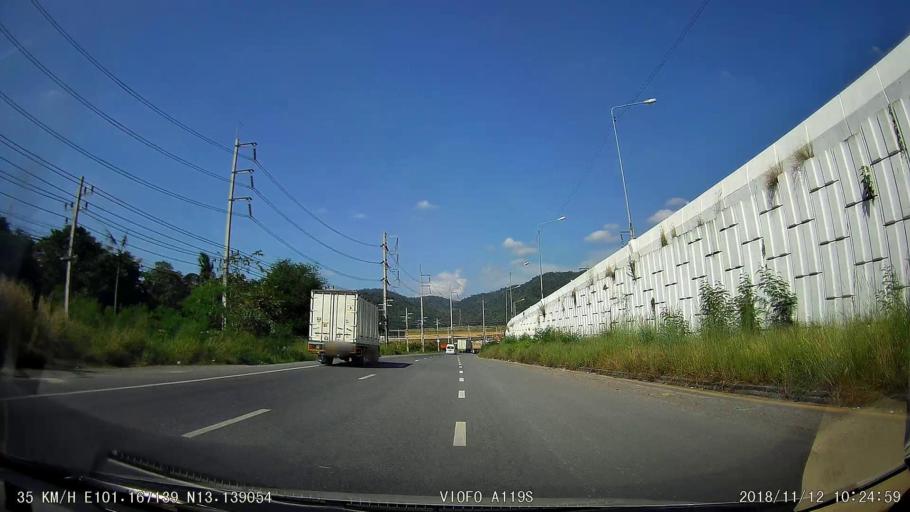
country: TH
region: Rayong
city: Pluak Daeng
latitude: 13.1391
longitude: 101.1670
